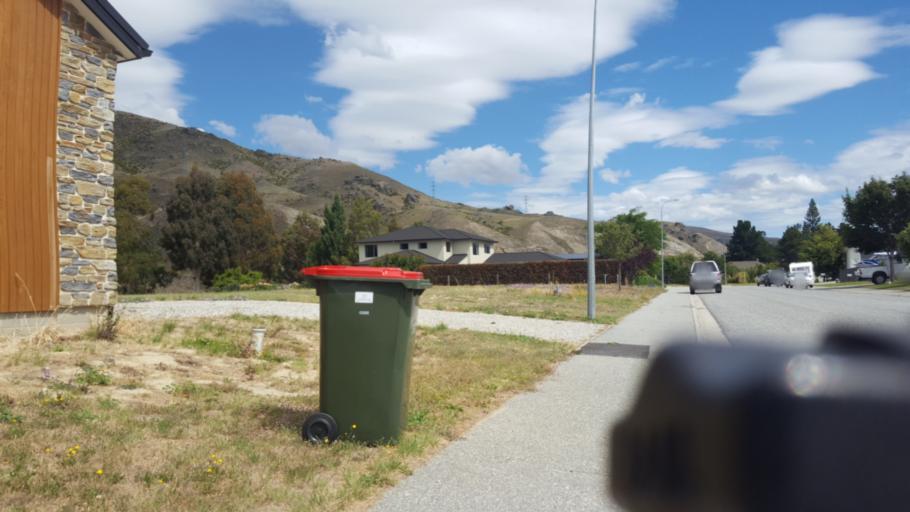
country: NZ
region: Otago
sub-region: Queenstown-Lakes District
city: Wanaka
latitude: -45.0390
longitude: 169.2182
